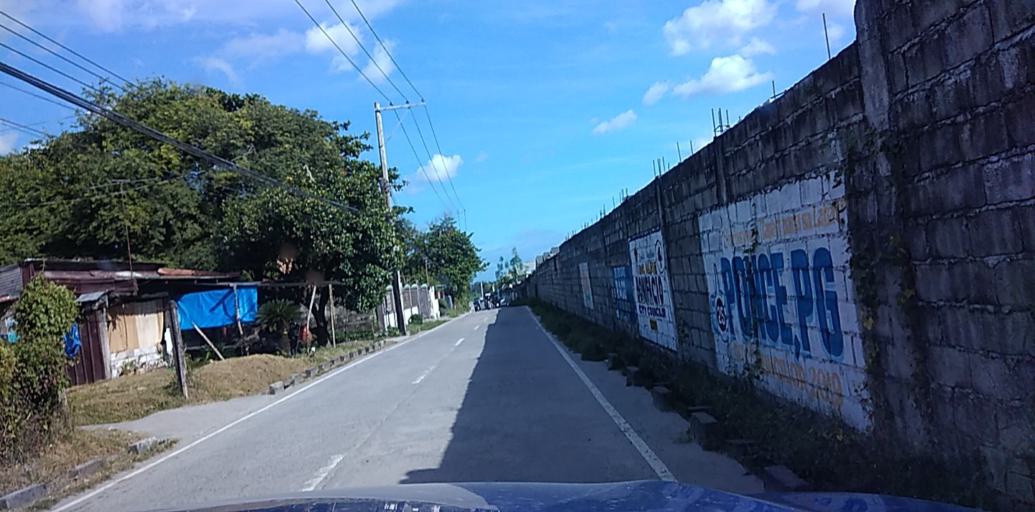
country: PH
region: Central Luzon
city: Santol
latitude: 15.1458
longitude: 120.5512
